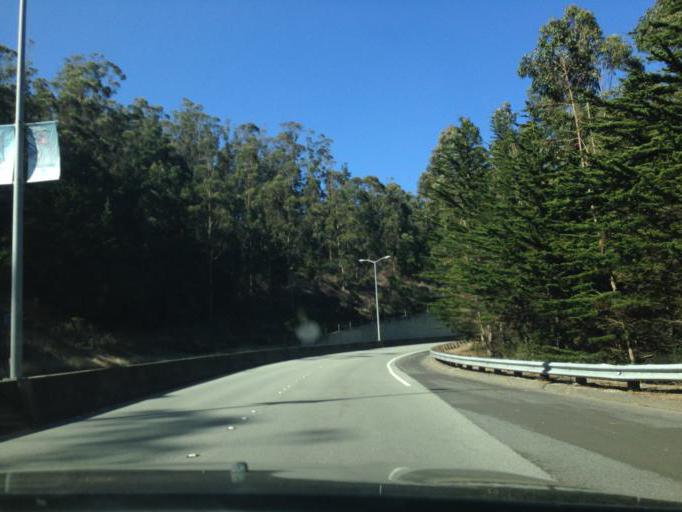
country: US
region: California
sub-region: San Mateo County
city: Pacifica
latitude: 37.6262
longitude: -122.4807
